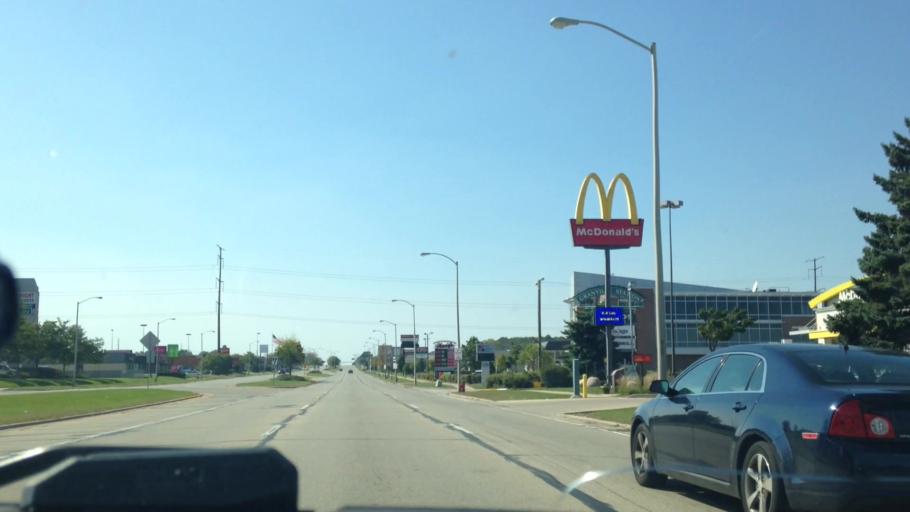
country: US
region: Wisconsin
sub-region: Milwaukee County
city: Brown Deer
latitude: 43.1779
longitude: -88.0105
